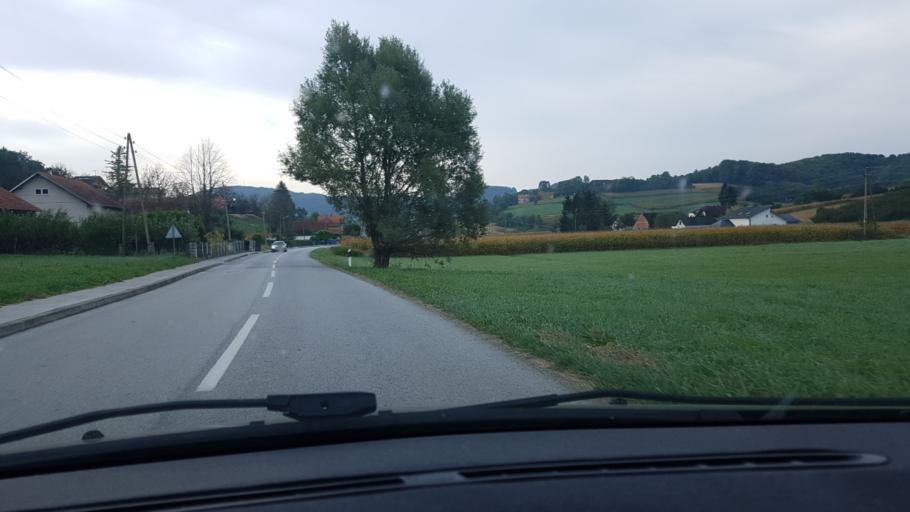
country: HR
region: Krapinsko-Zagorska
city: Mihovljan
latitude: 46.1398
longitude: 15.9642
